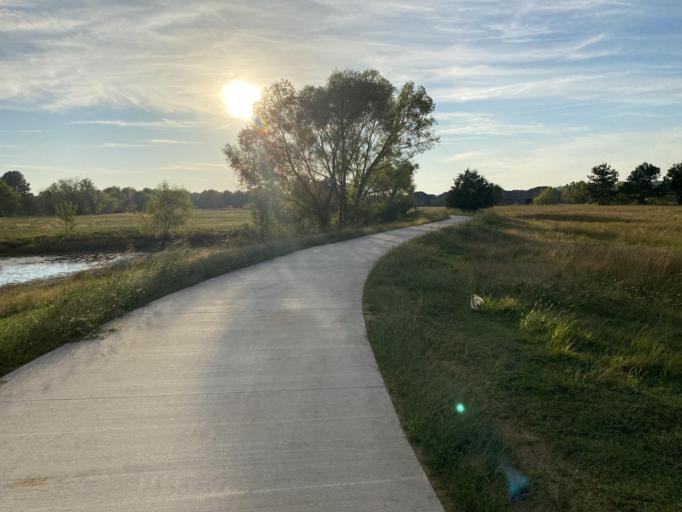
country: US
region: Arkansas
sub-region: Washington County
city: Johnson
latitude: 36.1046
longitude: -94.1971
